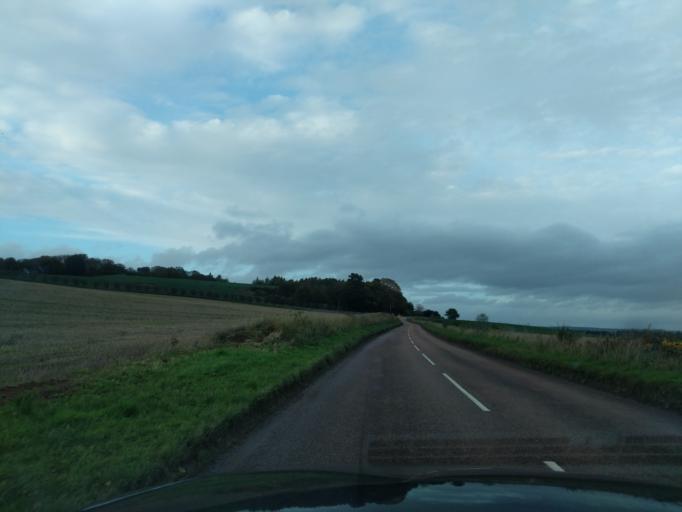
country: GB
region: Scotland
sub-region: Fife
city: Tayport
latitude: 56.4254
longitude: -2.8884
